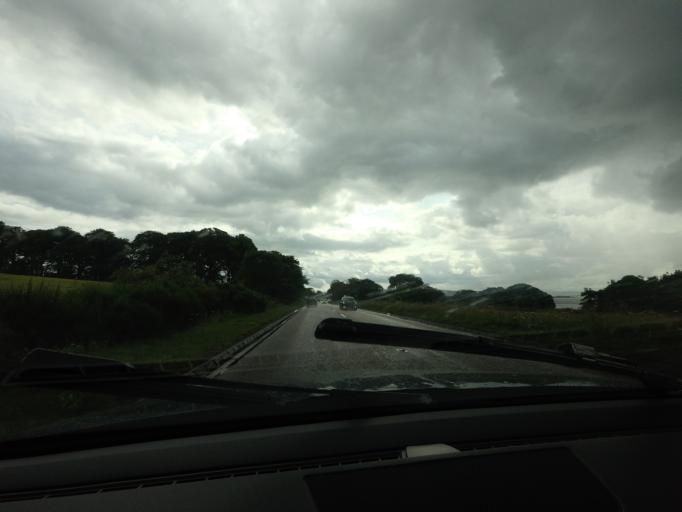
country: GB
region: Scotland
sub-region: Highland
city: Inverness
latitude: 57.4969
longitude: -4.1500
